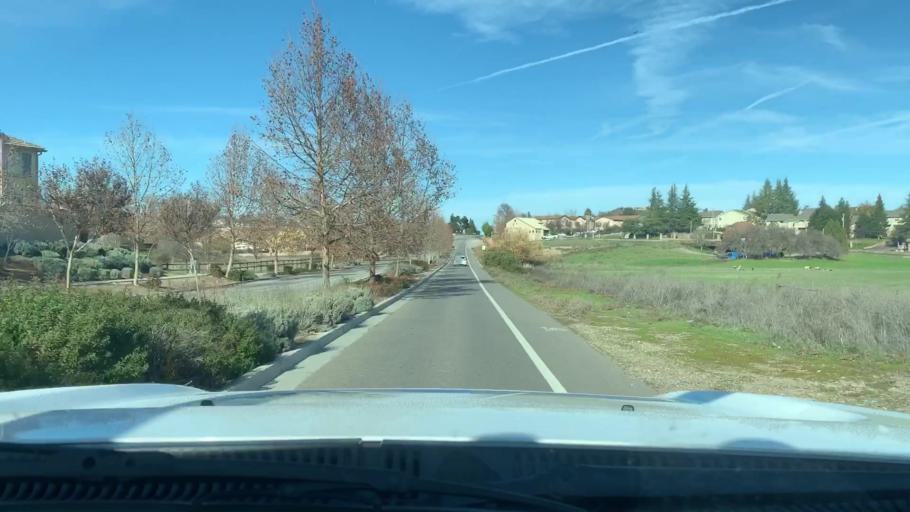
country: US
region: California
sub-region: San Luis Obispo County
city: Atascadero
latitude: 35.4521
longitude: -120.6372
